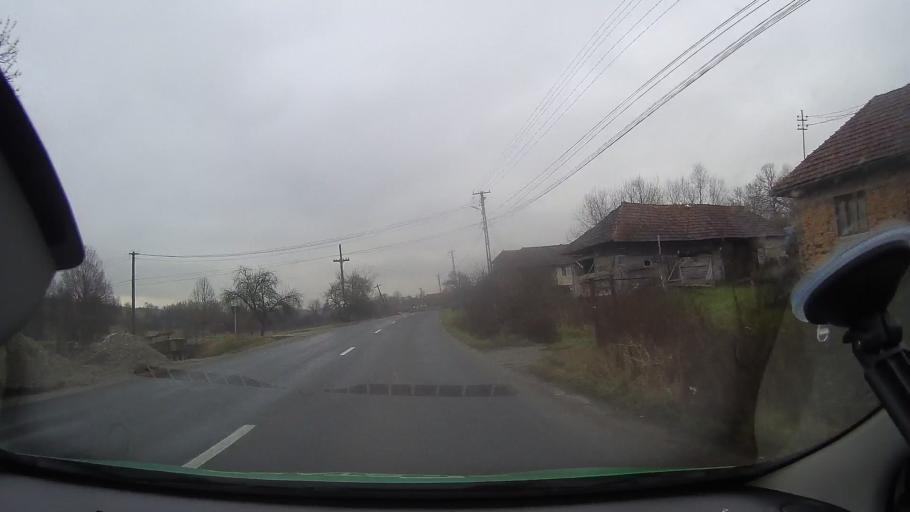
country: RO
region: Arad
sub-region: Comuna Varfurile
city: Varfurile
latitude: 46.3203
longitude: 22.5067
